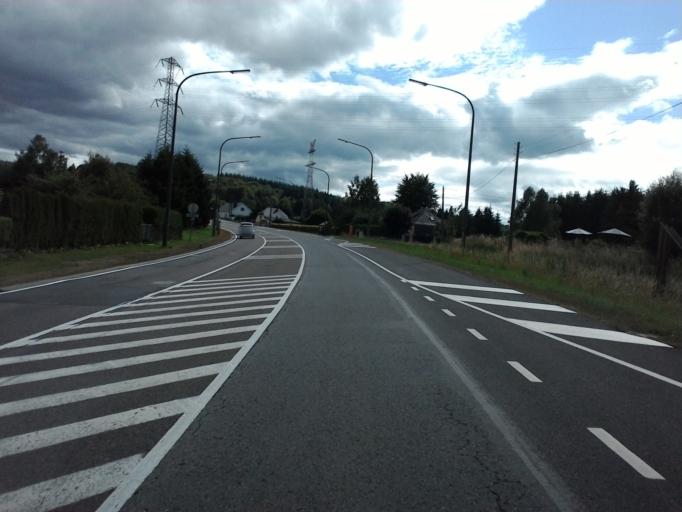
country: BE
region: Wallonia
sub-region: Province du Luxembourg
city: Martelange
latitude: 49.8207
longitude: 5.7427
